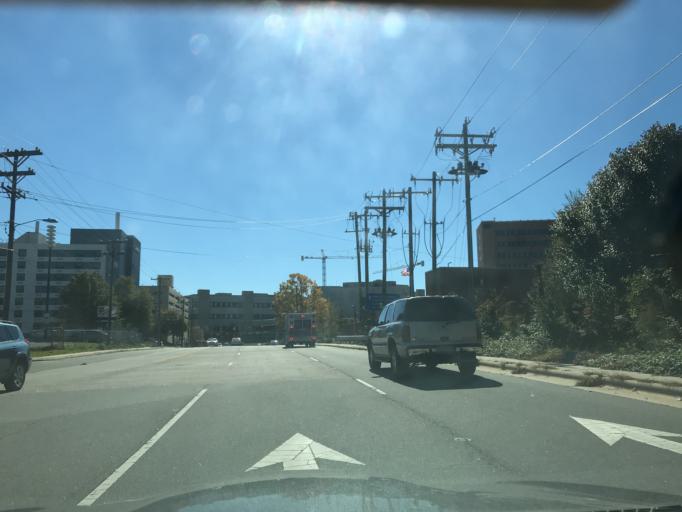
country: US
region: North Carolina
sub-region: Durham County
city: Durham
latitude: 36.0109
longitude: -78.9372
